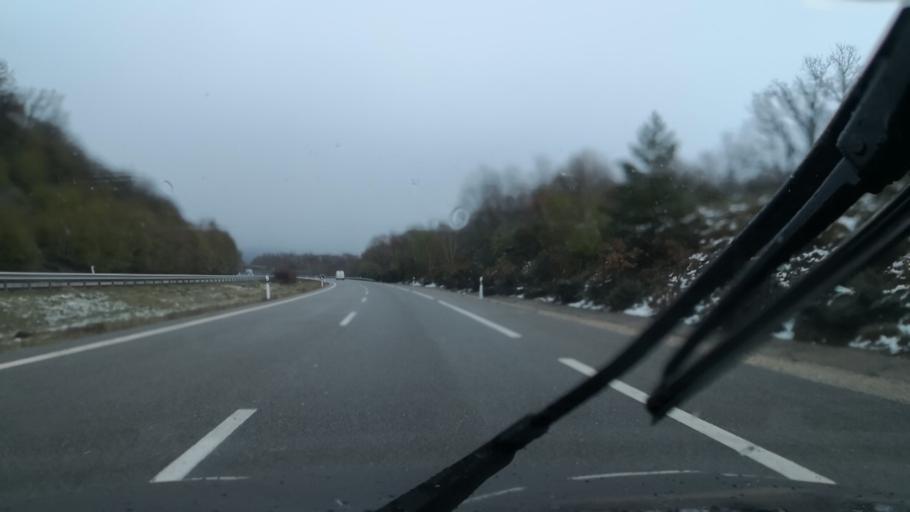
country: ES
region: Castille and Leon
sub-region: Provincia de Zamora
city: Requejo
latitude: 42.0342
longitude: -6.7323
